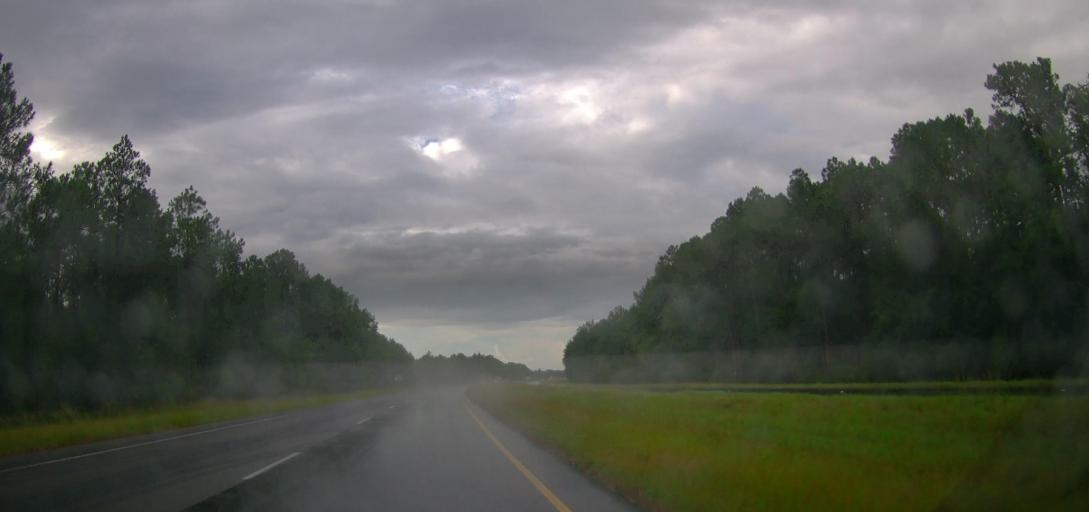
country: US
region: Georgia
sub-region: Ware County
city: Deenwood
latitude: 31.2172
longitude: -82.4218
